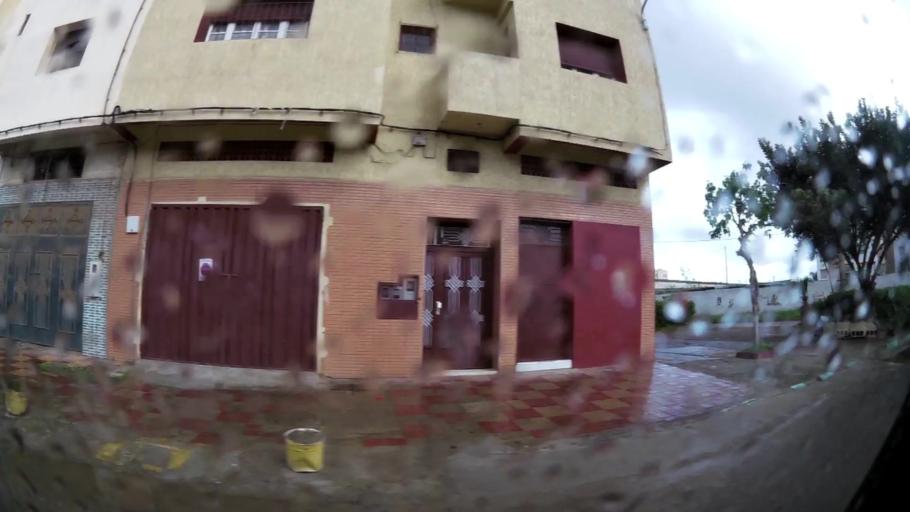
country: MA
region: Grand Casablanca
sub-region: Mohammedia
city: Mohammedia
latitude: 33.6741
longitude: -7.3958
